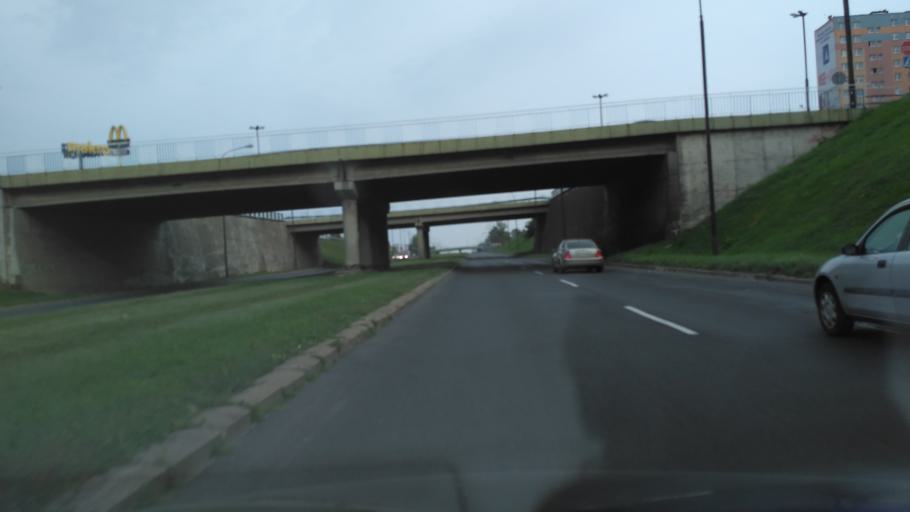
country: PL
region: Lublin Voivodeship
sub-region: Powiat lubelski
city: Lublin
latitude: 51.2370
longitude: 22.5945
